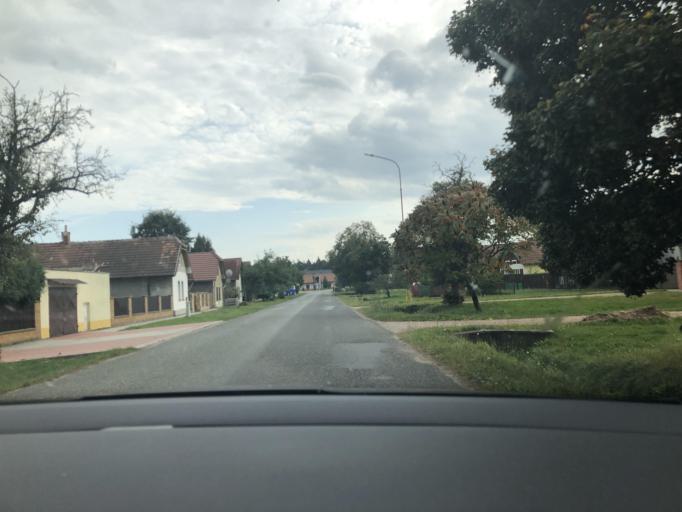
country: CZ
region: Pardubicky
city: Chvaletice
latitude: 50.0818
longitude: 15.4450
